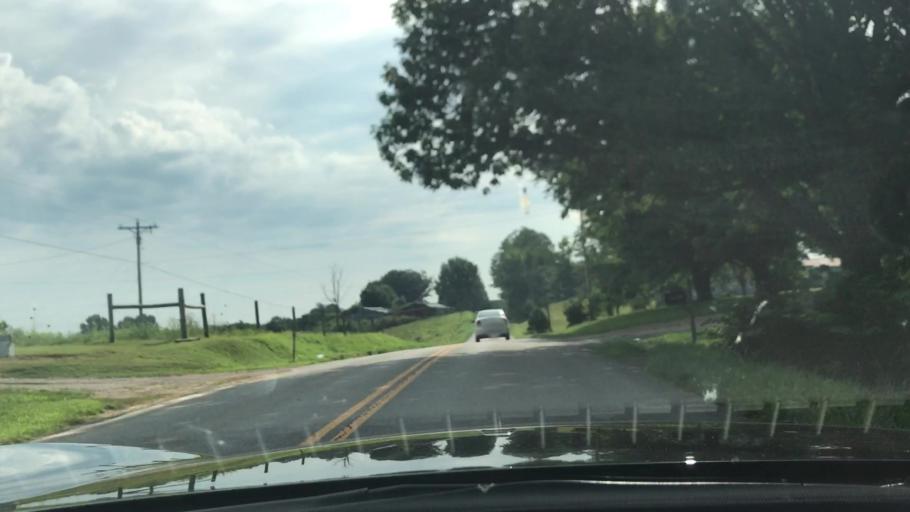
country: US
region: Kentucky
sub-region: Green County
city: Greensburg
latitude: 37.2623
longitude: -85.5547
